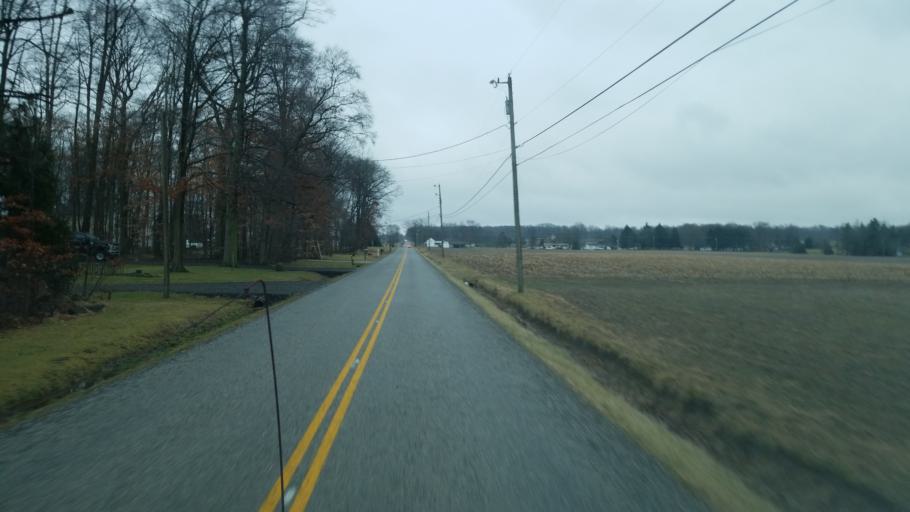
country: US
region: Ohio
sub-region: Wayne County
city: Orrville
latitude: 40.8786
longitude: -81.7837
